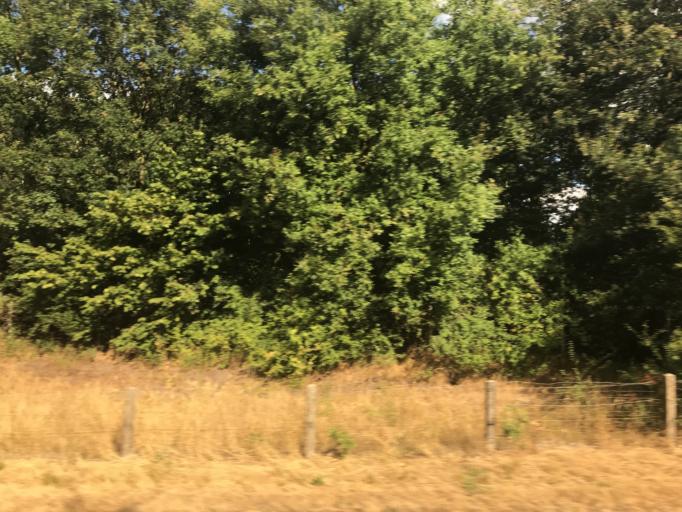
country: NL
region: Overijssel
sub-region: Gemeente Hof van Twente
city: Markelo
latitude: 52.3029
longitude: 6.4917
